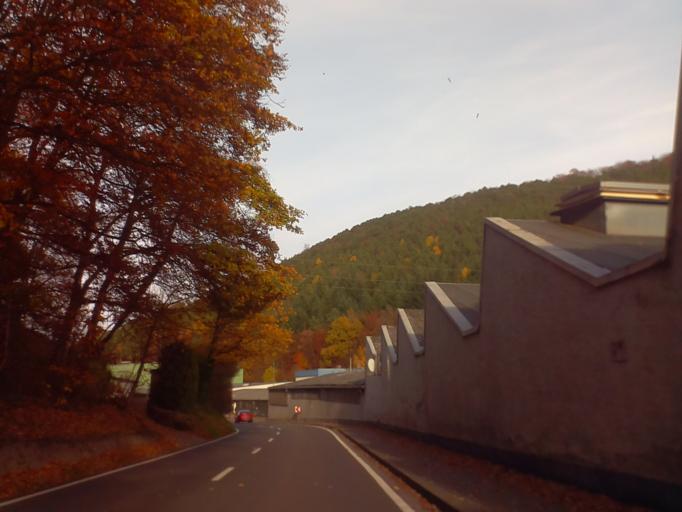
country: DE
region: Rheinland-Pfalz
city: Tiefenthal
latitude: 49.5205
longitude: 8.1010
